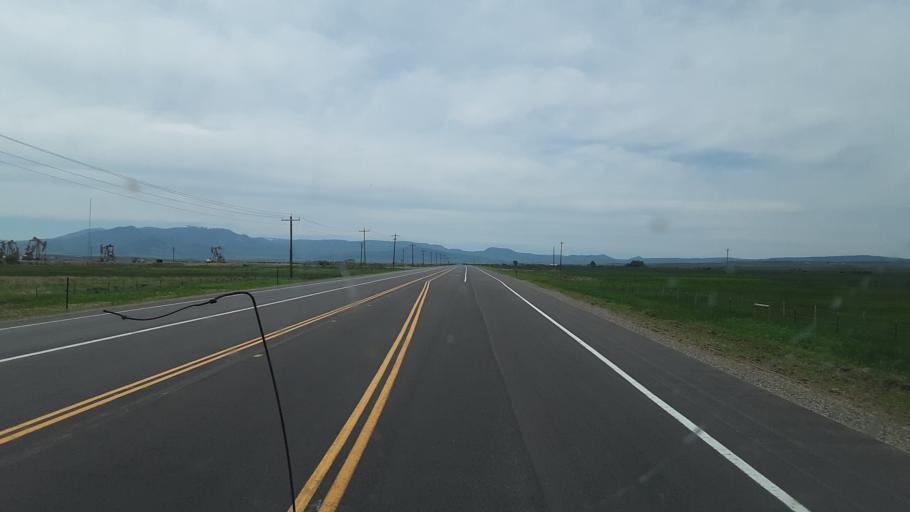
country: US
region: Colorado
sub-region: Jackson County
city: Walden
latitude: 40.5877
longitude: -106.4071
